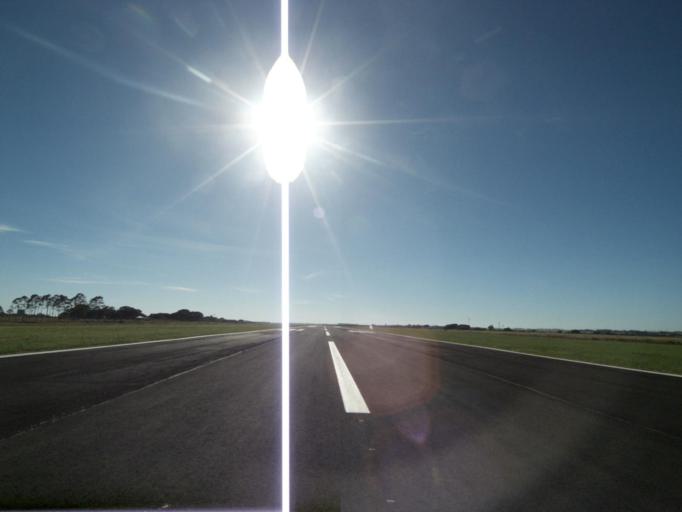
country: BR
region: Rio Grande do Sul
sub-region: Uruguaiana
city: Uruguaiana
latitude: -29.7826
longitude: -57.0448
